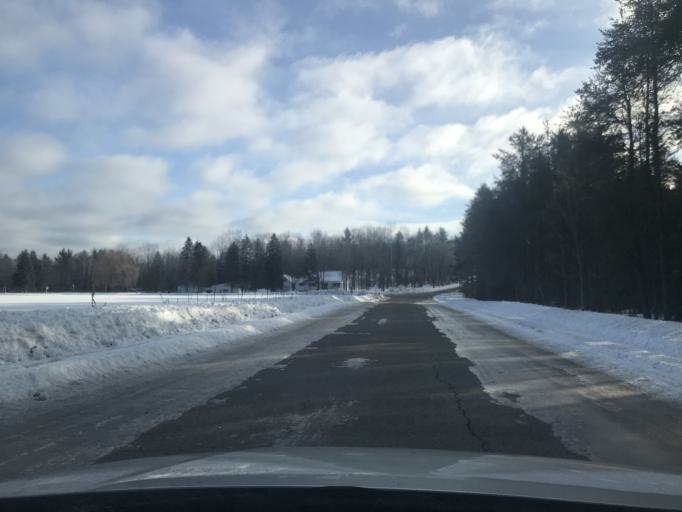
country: US
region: Wisconsin
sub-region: Marinette County
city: Niagara
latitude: 45.6261
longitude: -87.9691
